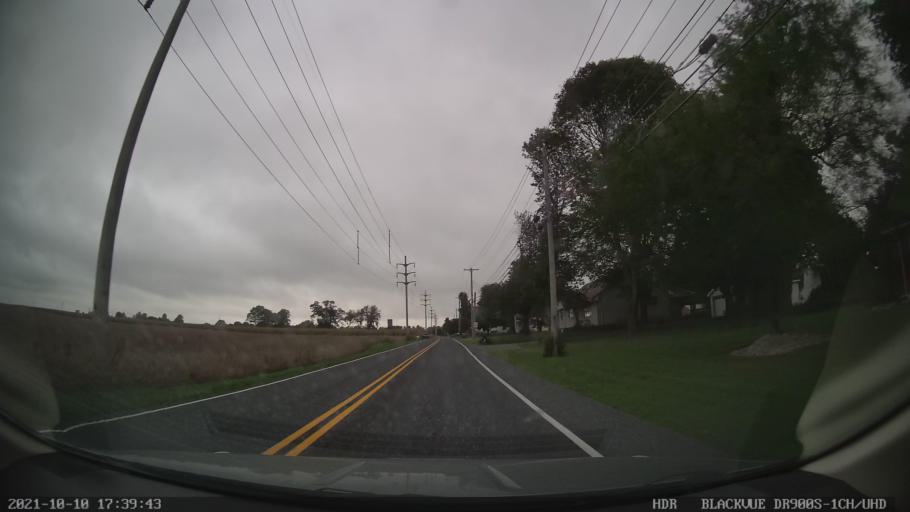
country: US
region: Pennsylvania
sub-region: Berks County
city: Topton
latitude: 40.5108
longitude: -75.6972
